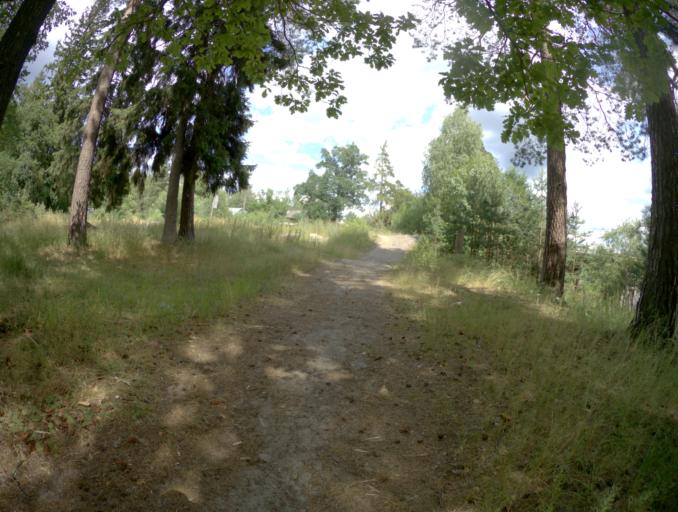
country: RU
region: Nizjnij Novgorod
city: Frolishchi
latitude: 56.4280
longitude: 42.6377
